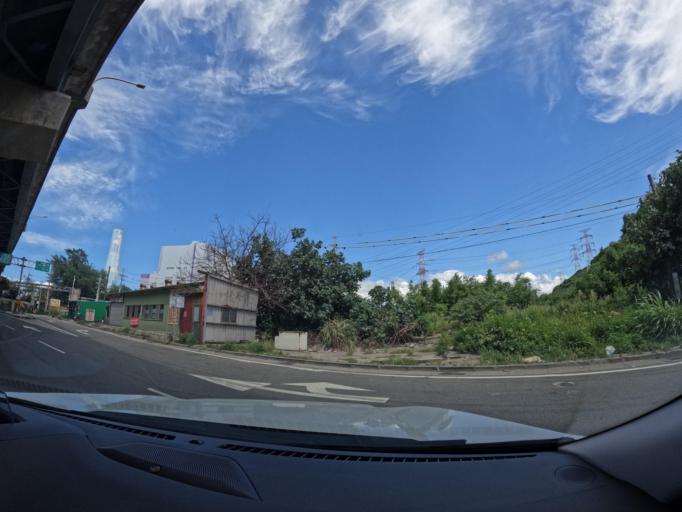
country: TW
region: Taiwan
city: Taoyuan City
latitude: 25.1201
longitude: 121.2957
